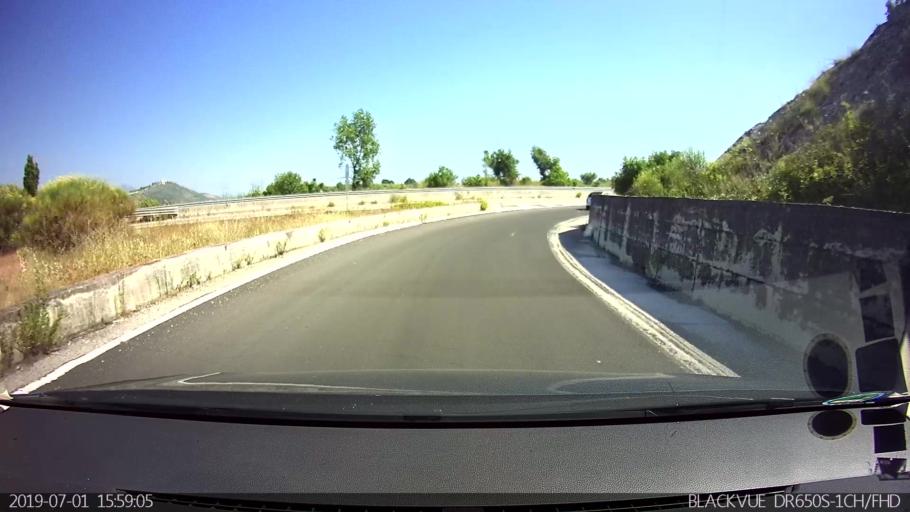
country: IT
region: Latium
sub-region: Provincia di Frosinone
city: Sant'Angelo in Villa-Giglio
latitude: 41.6634
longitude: 13.4246
